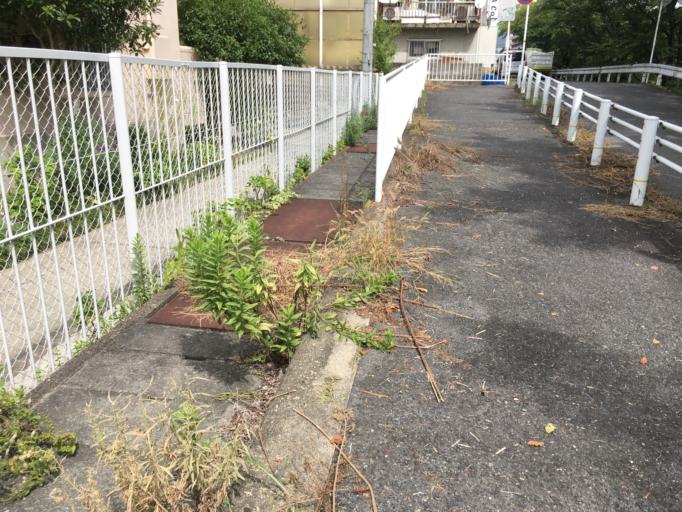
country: JP
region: Nara
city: Nara-shi
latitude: 34.6809
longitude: 135.8069
